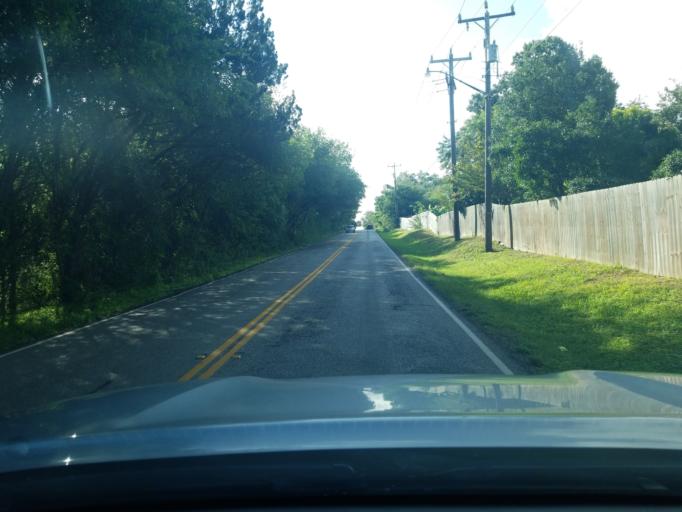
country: US
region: Texas
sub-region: Bexar County
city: Live Oak
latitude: 29.5936
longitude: -98.3588
